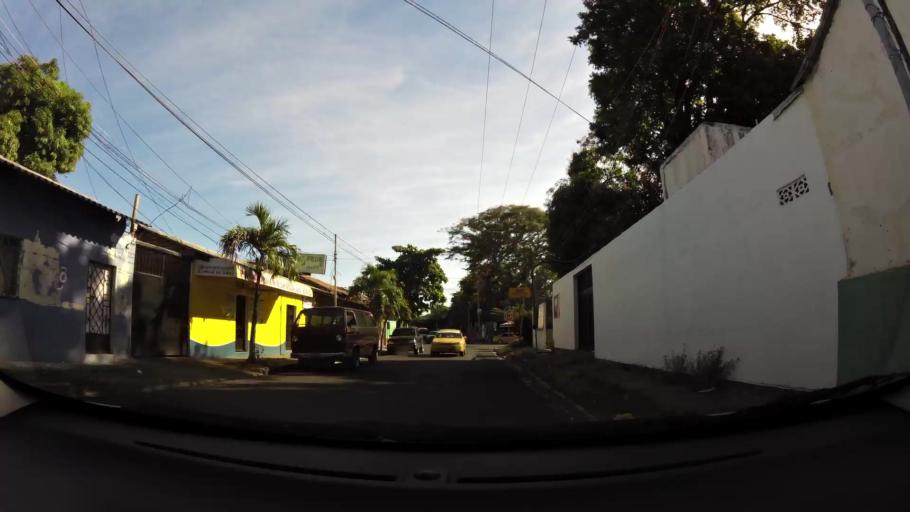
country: SV
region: San Miguel
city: San Miguel
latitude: 13.4754
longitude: -88.1897
